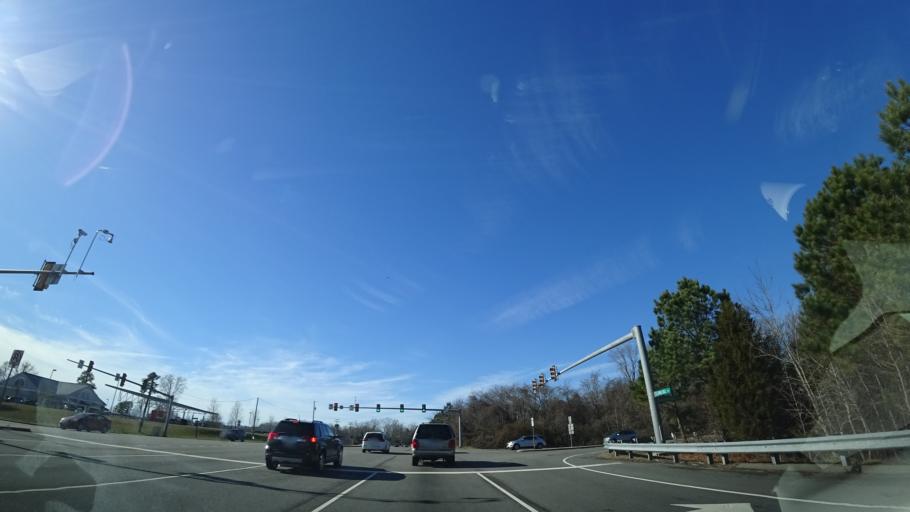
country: US
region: Virginia
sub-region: Henrico County
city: Glen Allen
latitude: 37.6874
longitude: -77.4594
